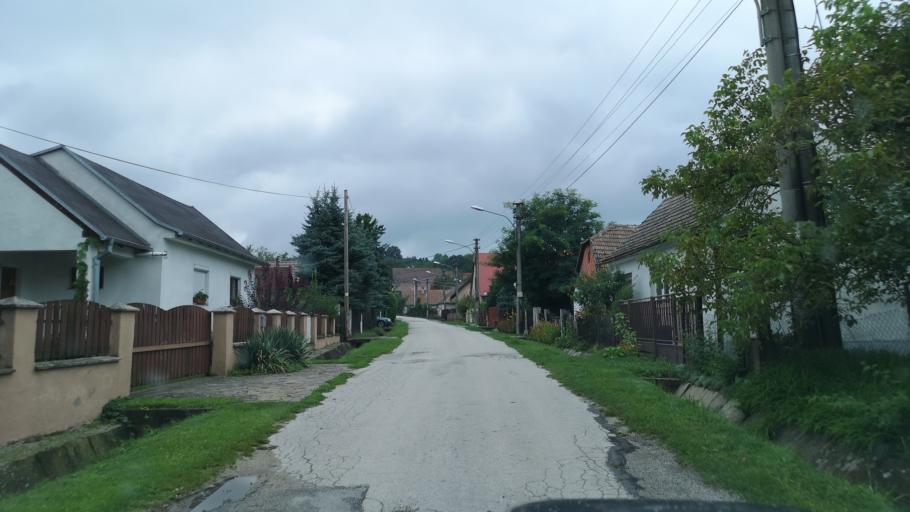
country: SK
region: Trnavsky
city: Smolenice
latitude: 48.5745
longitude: 17.4005
